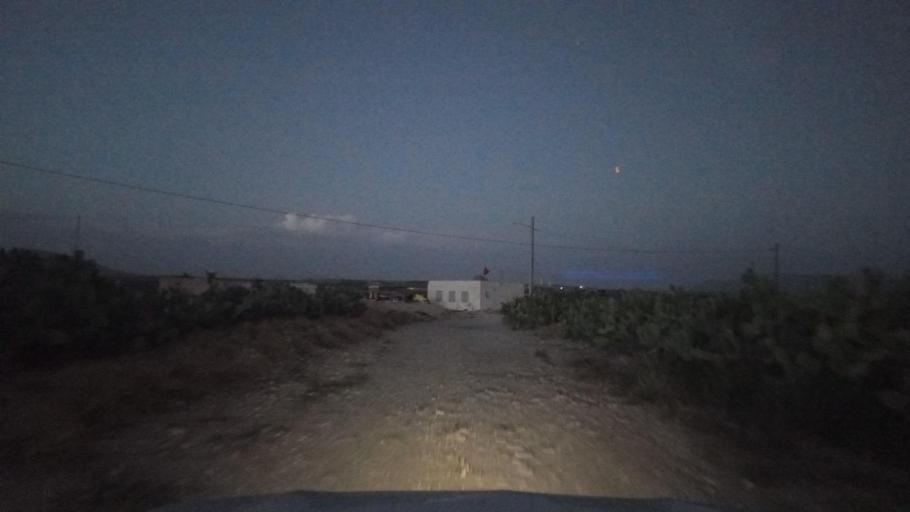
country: TN
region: Al Qasrayn
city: Sbiba
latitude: 35.3807
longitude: 9.0277
